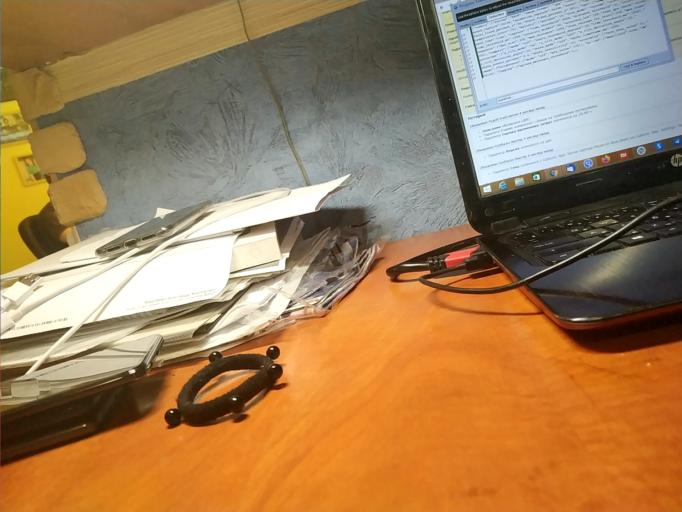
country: RU
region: Vologda
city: Ustyuzhna
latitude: 58.6673
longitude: 36.4262
